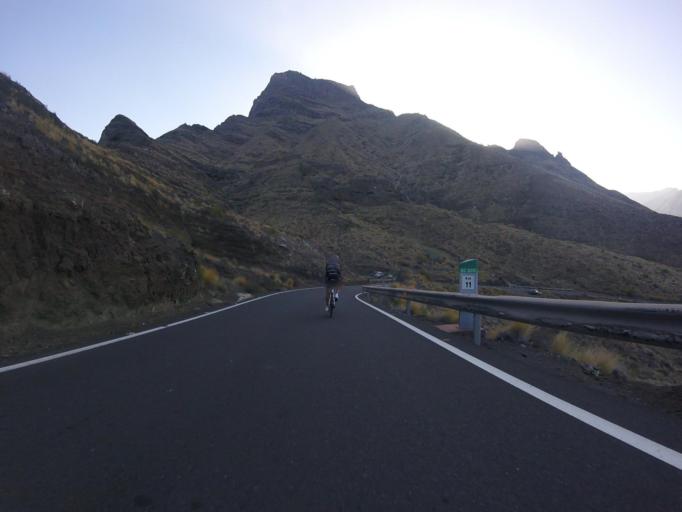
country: ES
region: Canary Islands
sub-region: Provincia de Las Palmas
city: Agaete
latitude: 28.0602
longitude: -15.7305
